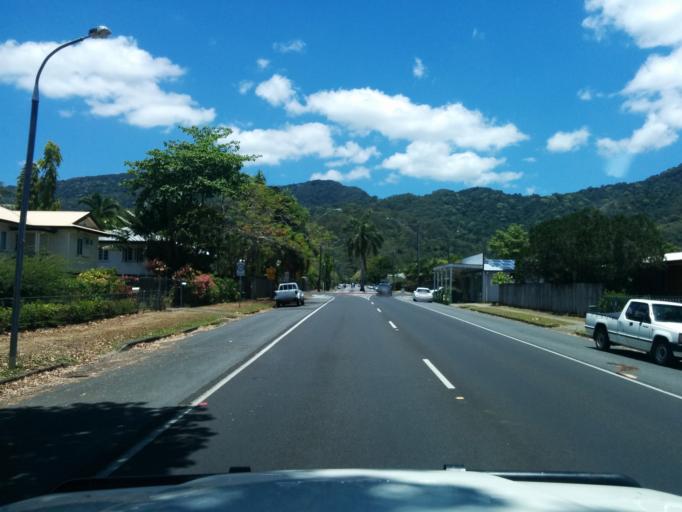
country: AU
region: Queensland
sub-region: Cairns
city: Woree
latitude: -16.9444
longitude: 145.7330
